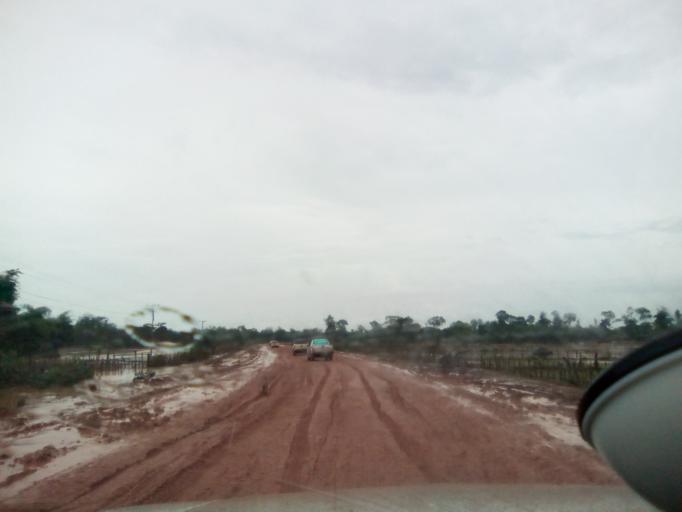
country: LA
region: Attapu
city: Attapu
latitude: 14.6951
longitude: 106.5329
